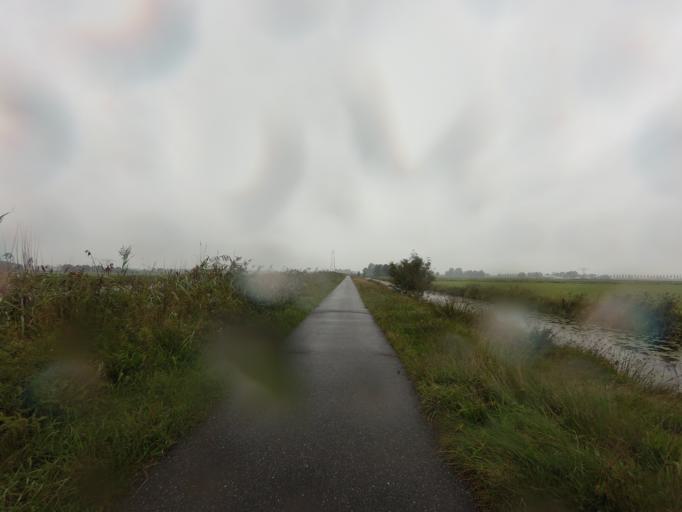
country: NL
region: Friesland
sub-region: Gemeente Boarnsterhim
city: Aldeboarn
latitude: 53.0084
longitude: 5.8896
